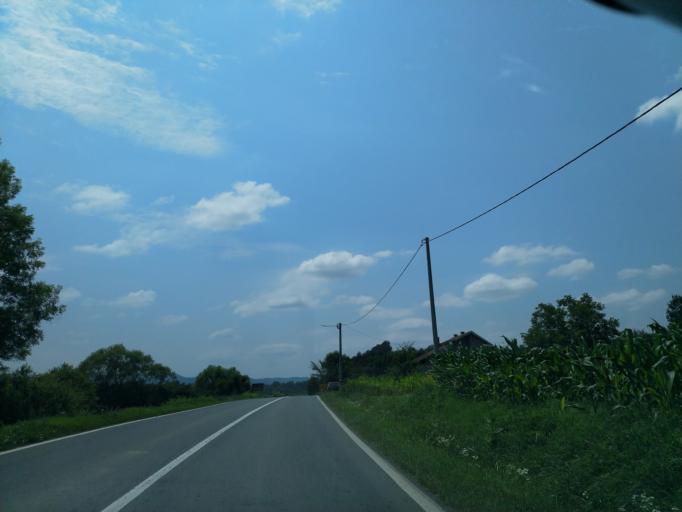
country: RS
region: Central Serbia
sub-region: Rasinski Okrug
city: Krusevac
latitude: 43.4859
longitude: 21.2772
